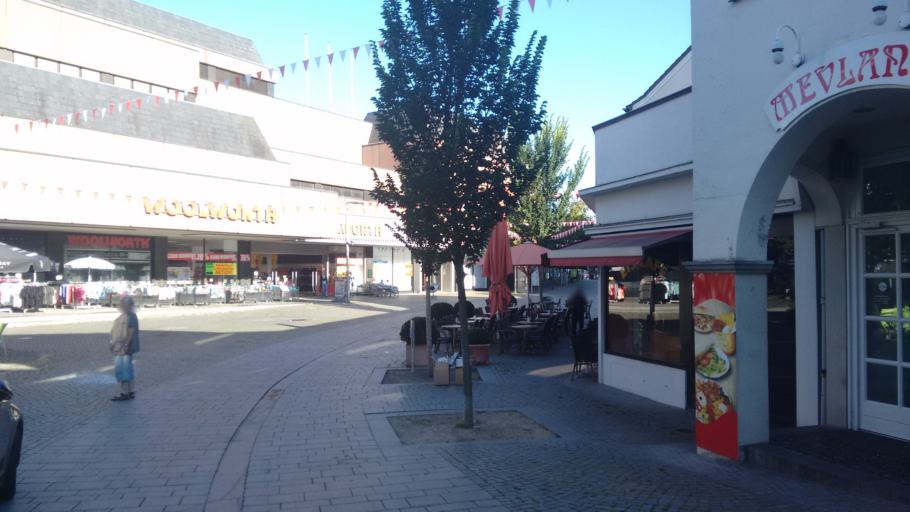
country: DE
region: North Rhine-Westphalia
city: Buende
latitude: 52.1961
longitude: 8.5817
